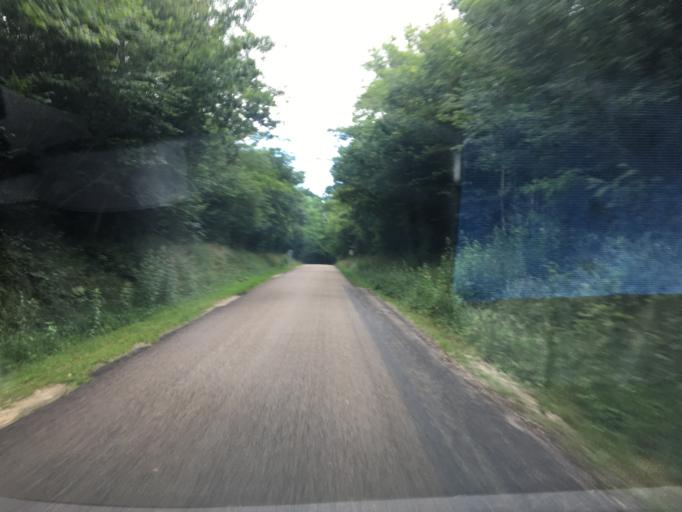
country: FR
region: Bourgogne
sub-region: Departement de l'Yonne
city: Fleury-la-Vallee
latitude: 47.8627
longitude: 3.4826
